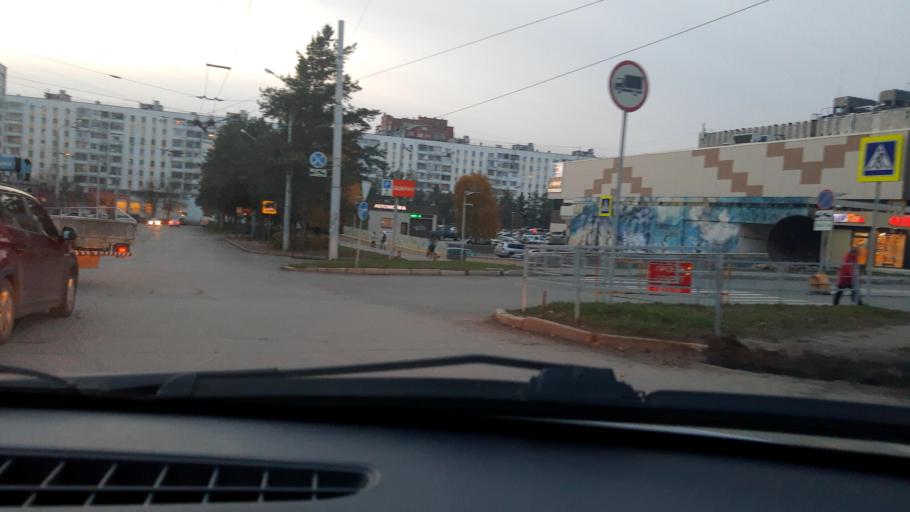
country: RU
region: Bashkortostan
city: Ufa
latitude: 54.7401
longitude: 56.0282
